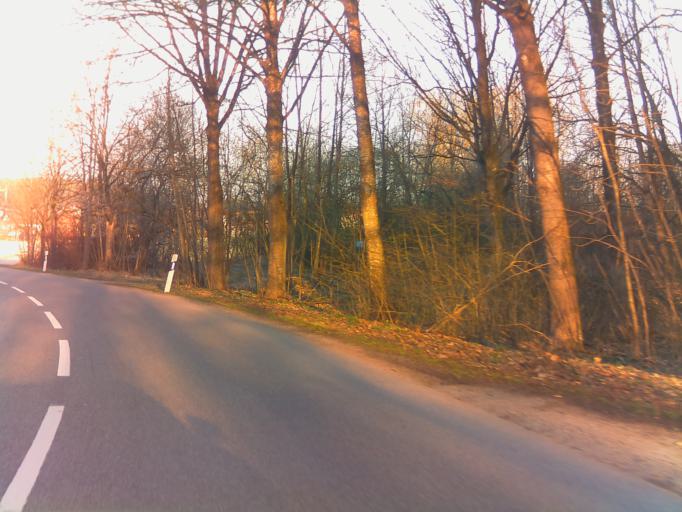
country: DE
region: Bavaria
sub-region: Upper Bavaria
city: Geltendorf
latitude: 48.1179
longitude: 11.0395
